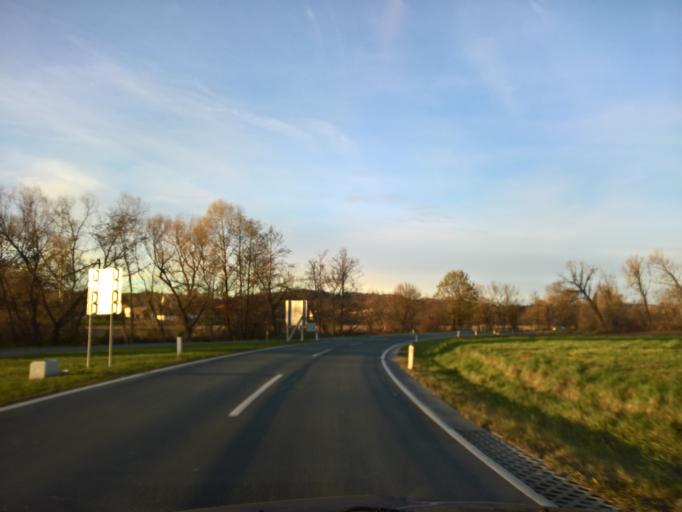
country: AT
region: Styria
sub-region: Politischer Bezirk Leibnitz
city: Sankt Johann im Saggautal
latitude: 46.7006
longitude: 15.3925
